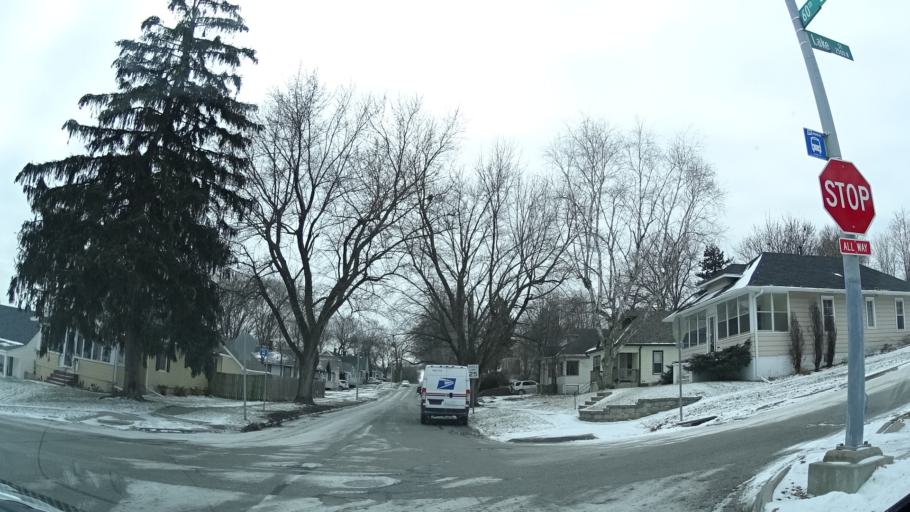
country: US
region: Nebraska
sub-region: Douglas County
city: Omaha
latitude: 41.2814
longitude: -96.0048
